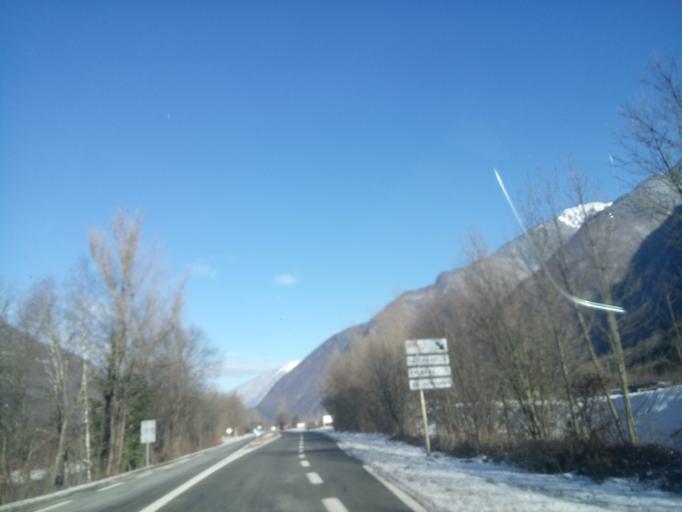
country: FR
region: Rhone-Alpes
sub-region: Departement de la Savoie
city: Saint-Remy-de-Maurienne
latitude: 45.4379
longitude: 6.2847
